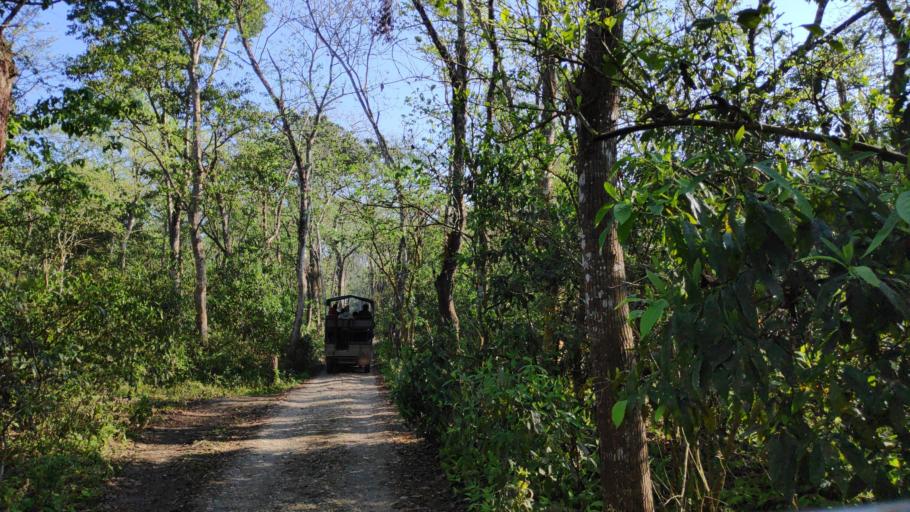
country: NP
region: Central Region
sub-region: Narayani Zone
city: Bharatpur
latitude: 27.5616
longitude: 84.5371
